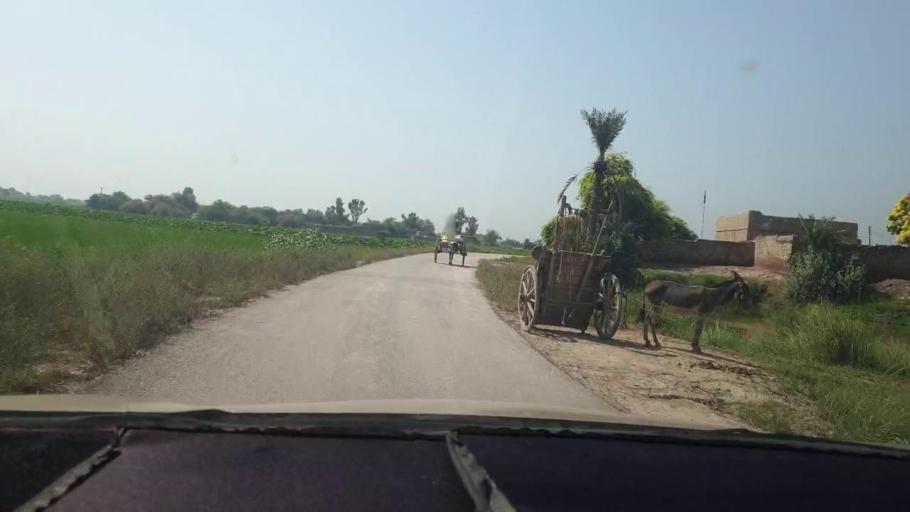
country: PK
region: Sindh
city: Kambar
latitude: 27.5613
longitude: 68.0438
